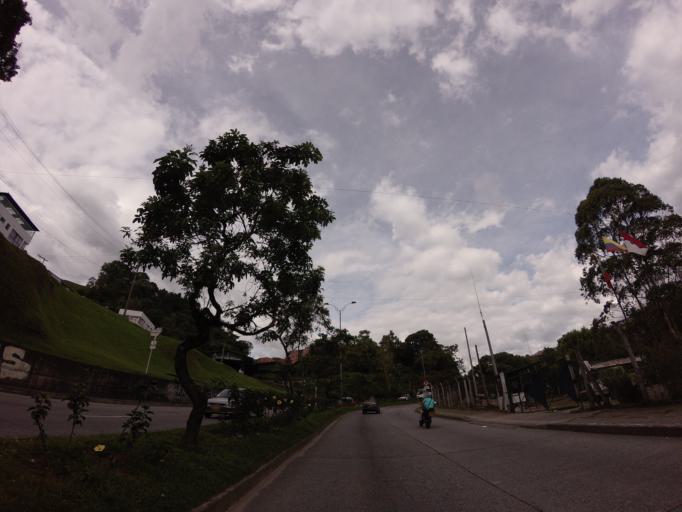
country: CO
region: Caldas
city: Manizales
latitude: 5.0709
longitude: -75.4998
